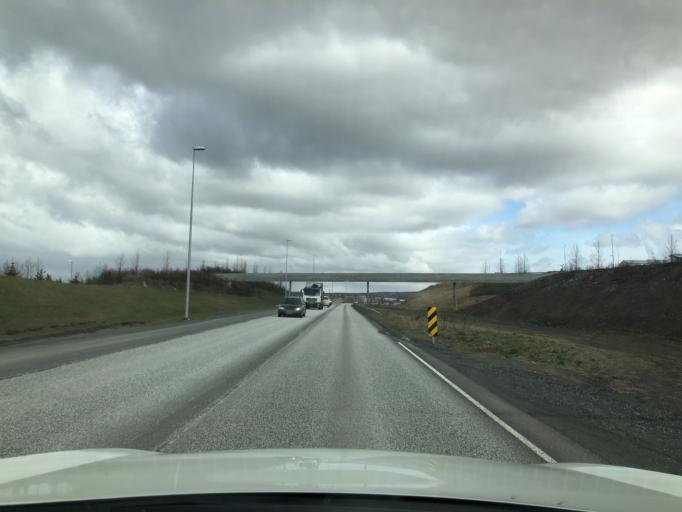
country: IS
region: Capital Region
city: Hafnarfjoerdur
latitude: 64.0577
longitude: -21.9539
